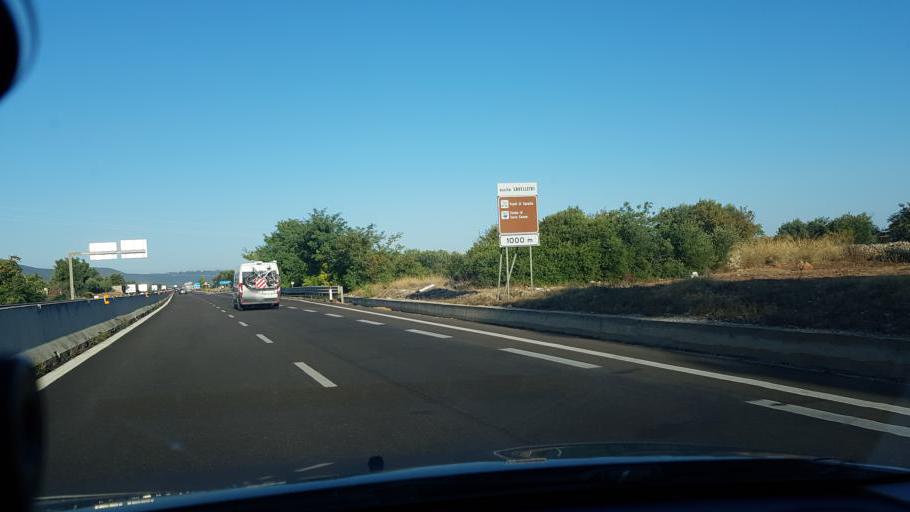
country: IT
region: Apulia
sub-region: Provincia di Brindisi
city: Fasano
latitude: 40.8367
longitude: 17.3844
